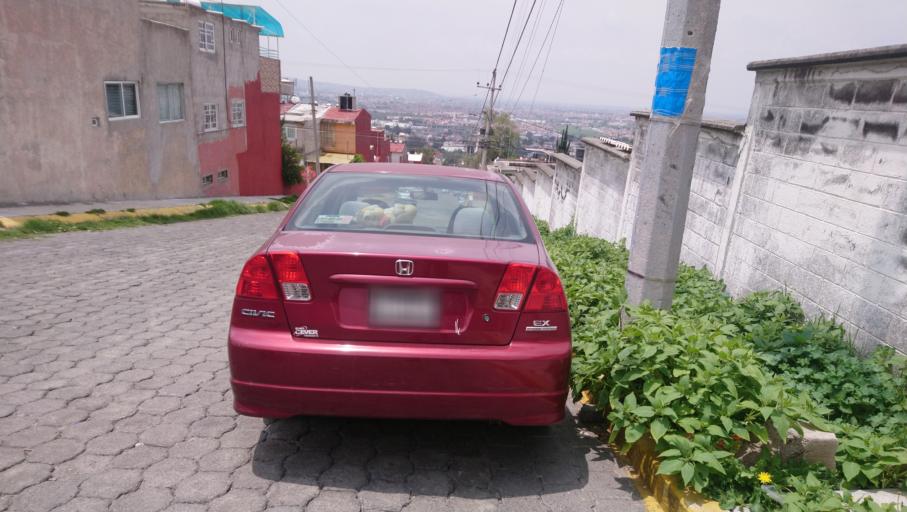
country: MX
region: Mexico
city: Coacalco
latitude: 19.6241
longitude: -99.1141
